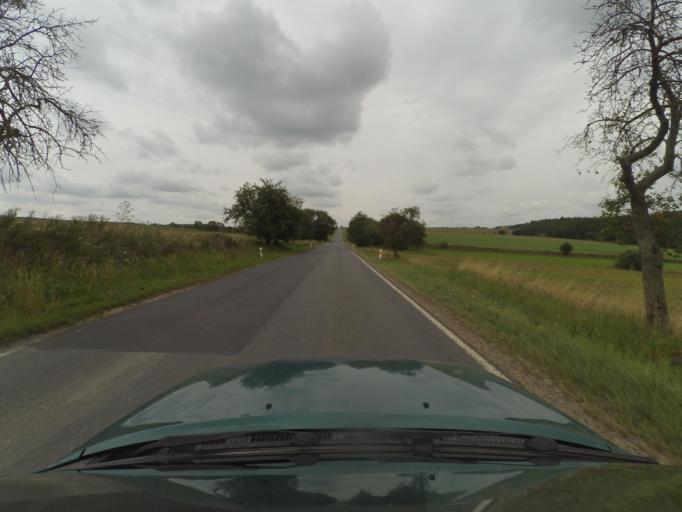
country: CZ
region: Plzensky
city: Kozlany
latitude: 50.0317
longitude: 13.5898
